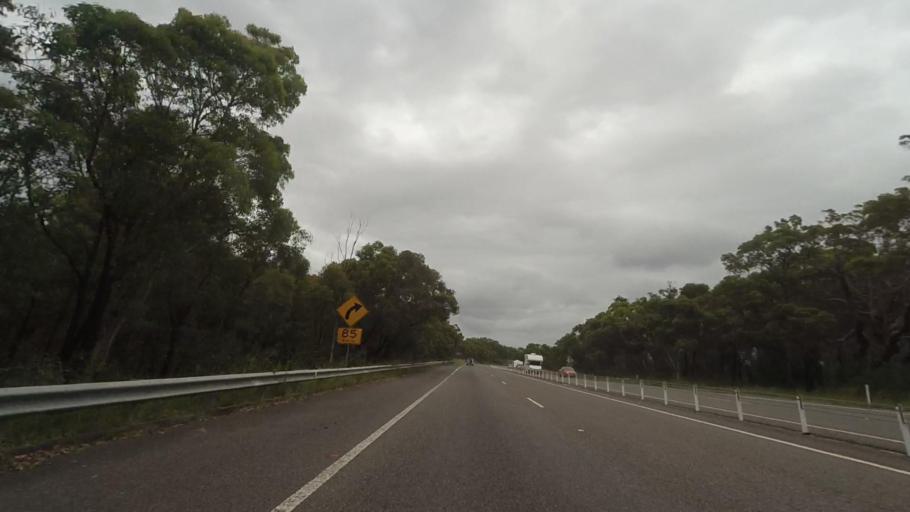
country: AU
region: New South Wales
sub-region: Wyong Shire
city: Kingfisher Shores
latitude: -33.1314
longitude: 151.6171
